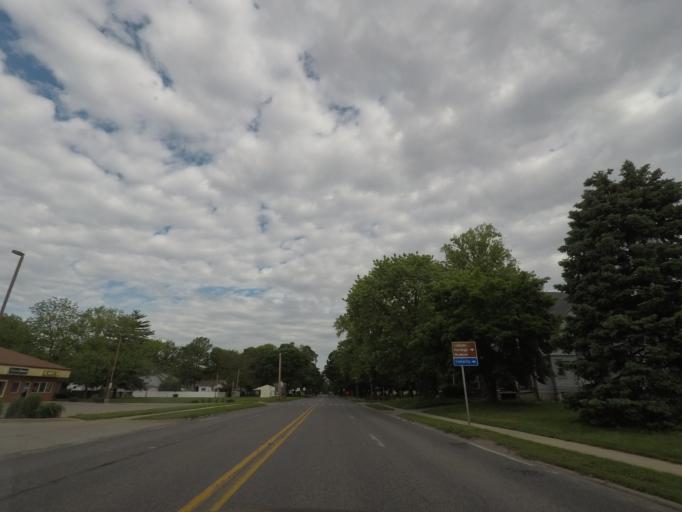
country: US
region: Illinois
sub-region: Logan County
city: Lincoln
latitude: 40.1543
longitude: -89.3613
